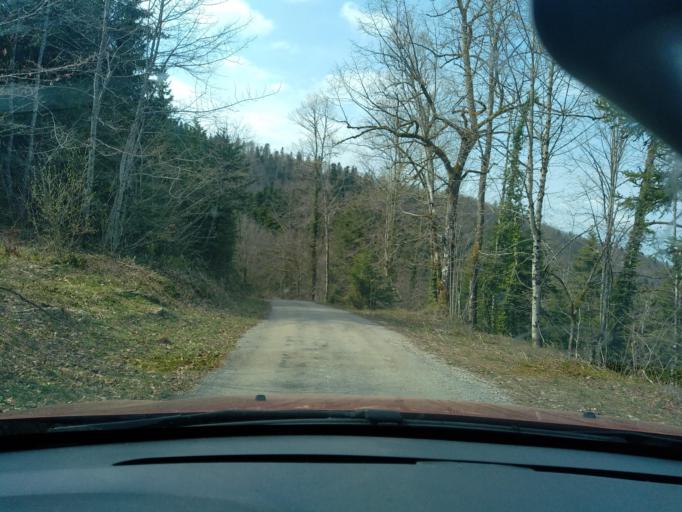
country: FR
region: Franche-Comte
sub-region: Departement du Jura
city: Moirans-en-Montagne
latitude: 46.4747
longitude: 5.7560
